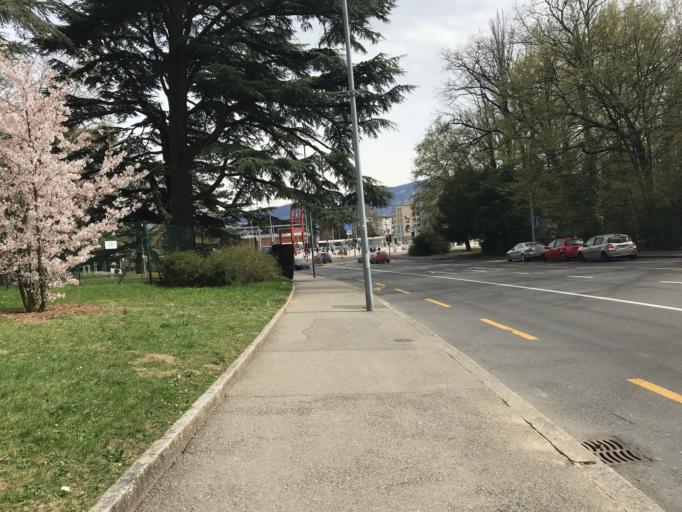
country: CH
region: Geneva
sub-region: Geneva
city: Le Grand-Saconnex
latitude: 46.2237
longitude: 6.1378
